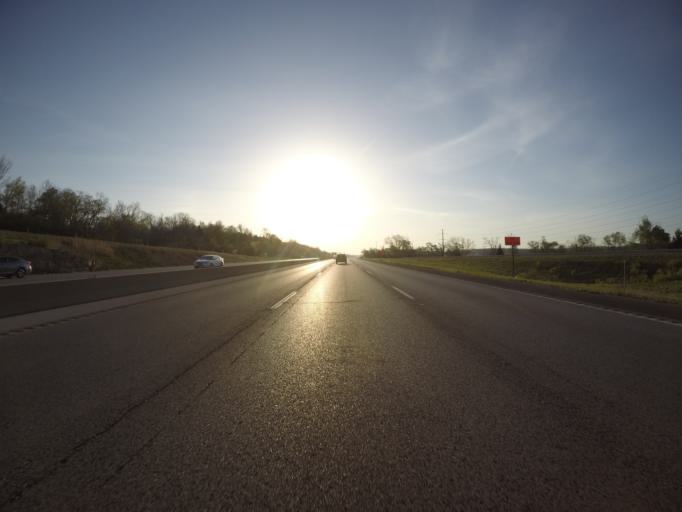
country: US
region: Missouri
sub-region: Jackson County
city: Raytown
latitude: 38.9376
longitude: -94.4700
